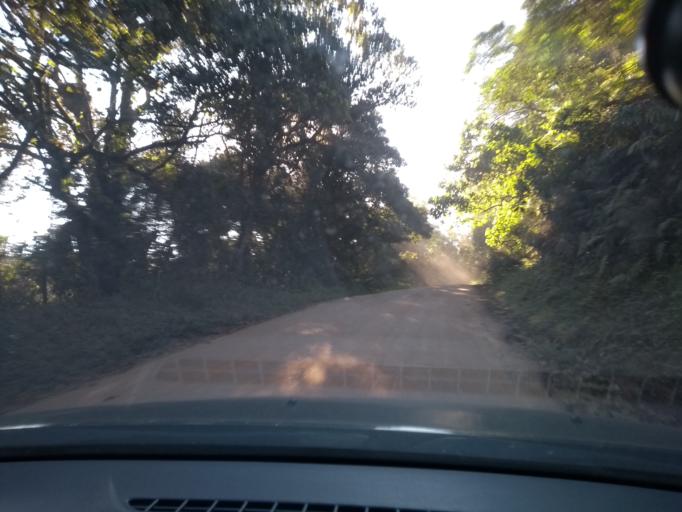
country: BR
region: Sao Paulo
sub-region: Sao Bernardo Do Campo
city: Sao Bernardo do Campo
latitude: -23.7747
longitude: -46.4991
